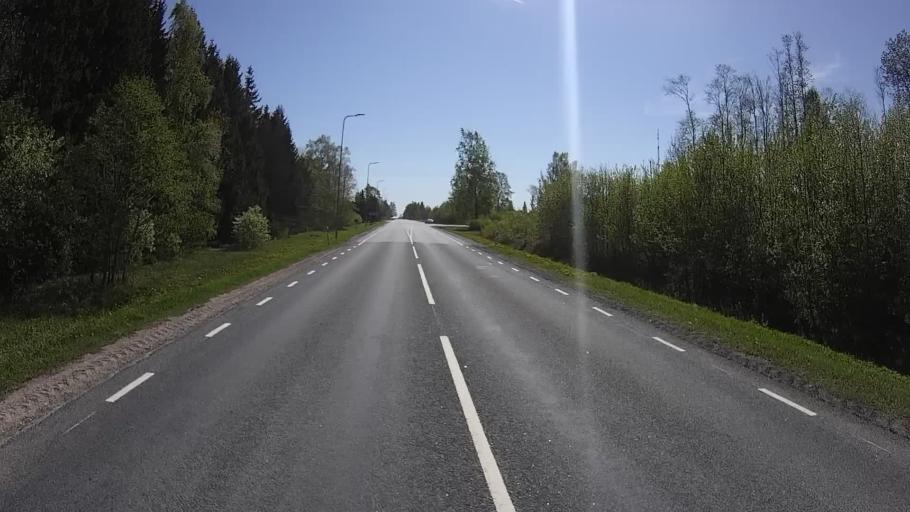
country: EE
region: Laeaene
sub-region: Lihula vald
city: Lihula
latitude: 58.5464
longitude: 23.9965
